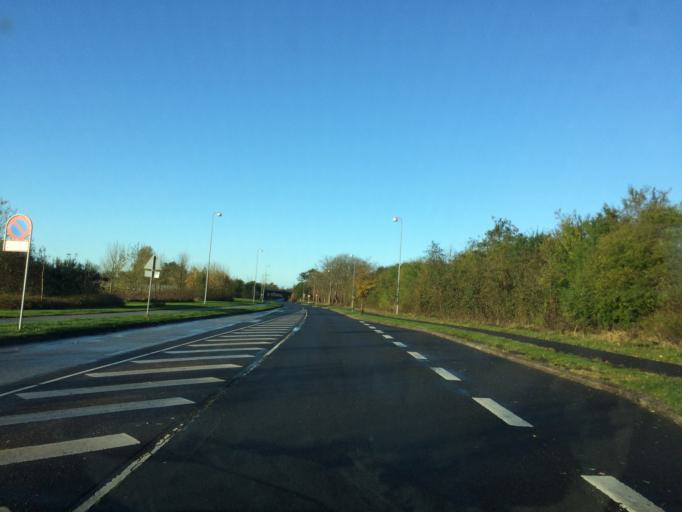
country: DK
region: South Denmark
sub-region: Fredericia Kommune
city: Taulov
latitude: 55.5526
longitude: 9.6429
